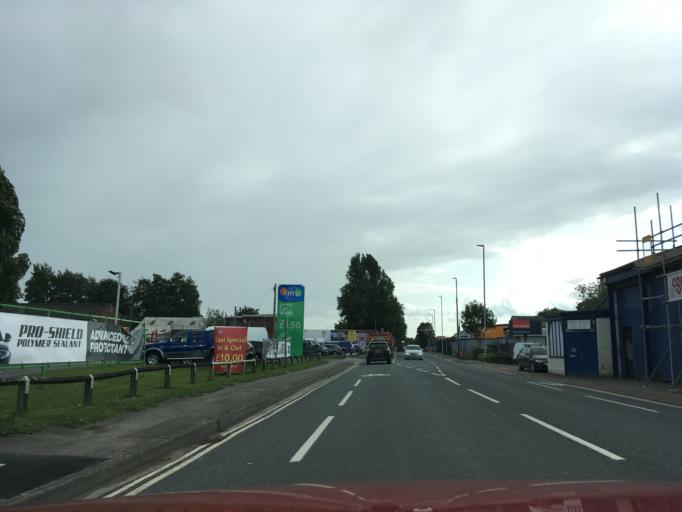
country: GB
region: England
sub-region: Gloucestershire
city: Gloucester
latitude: 51.8440
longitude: -2.2648
